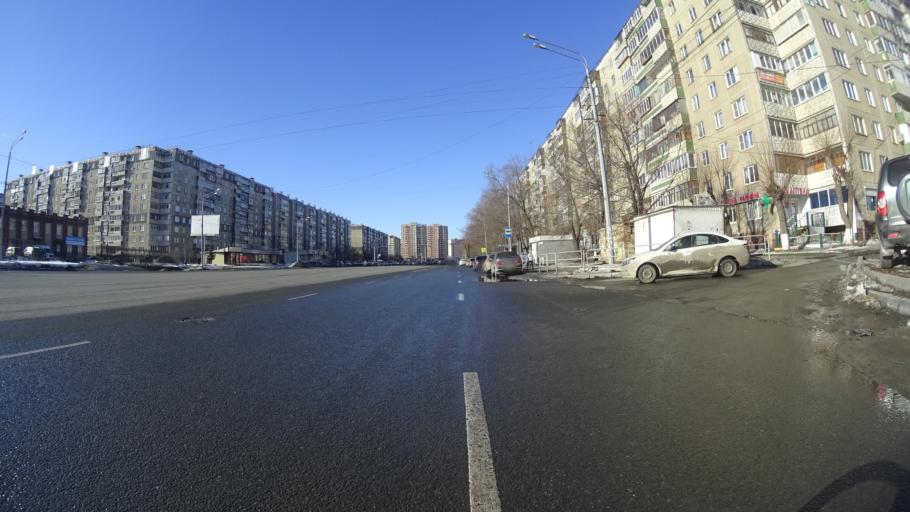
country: RU
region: Chelyabinsk
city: Roshchino
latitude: 55.1879
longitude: 61.2855
